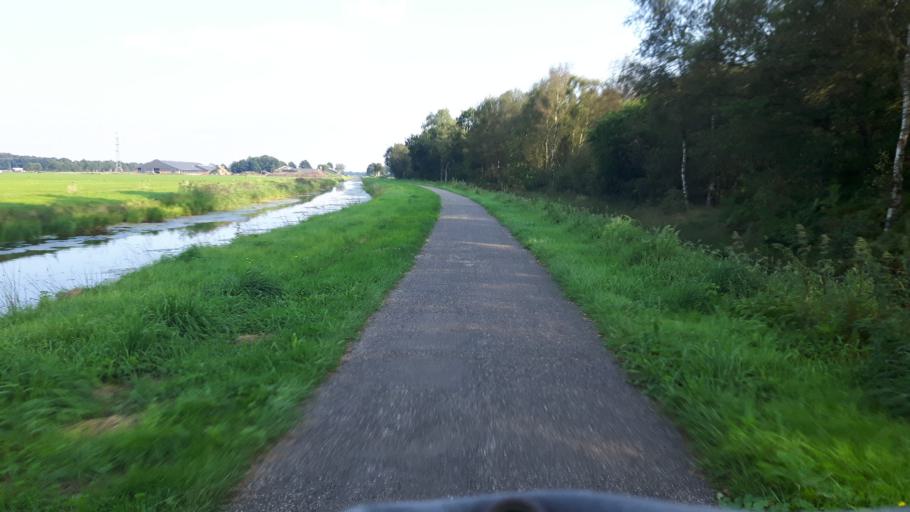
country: NL
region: Drenthe
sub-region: Gemeente Tynaarlo
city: Vries
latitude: 53.1220
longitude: 6.4994
